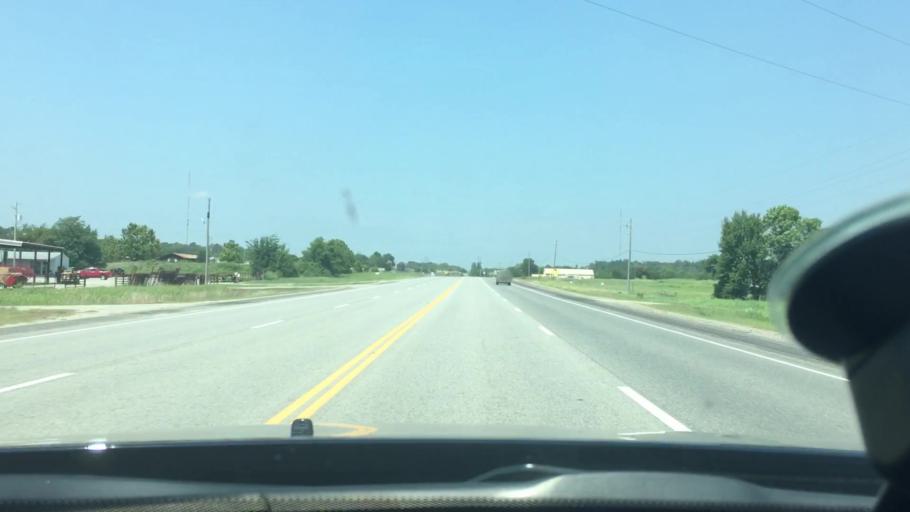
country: US
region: Oklahoma
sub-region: Atoka County
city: Atoka
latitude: 34.3667
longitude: -96.1014
